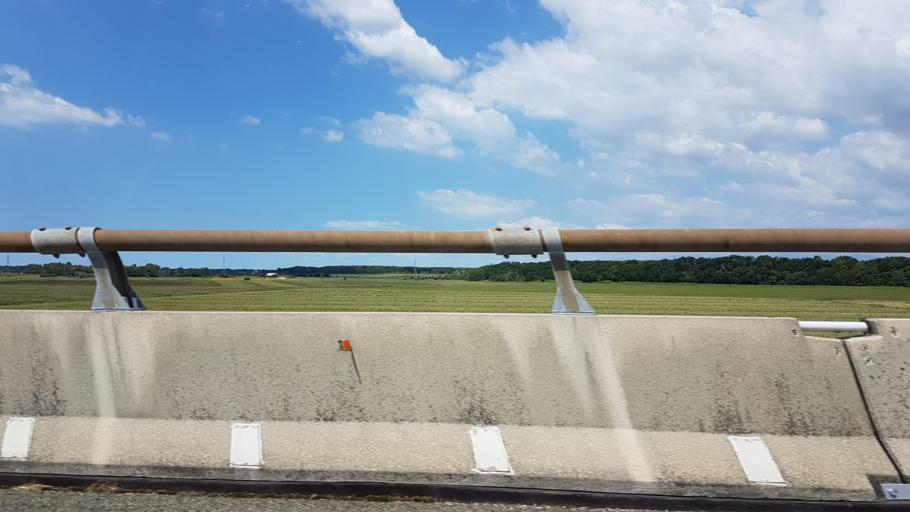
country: IT
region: Tuscany
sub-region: Provincia di Livorno
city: Guasticce
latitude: 43.6171
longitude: 10.3985
